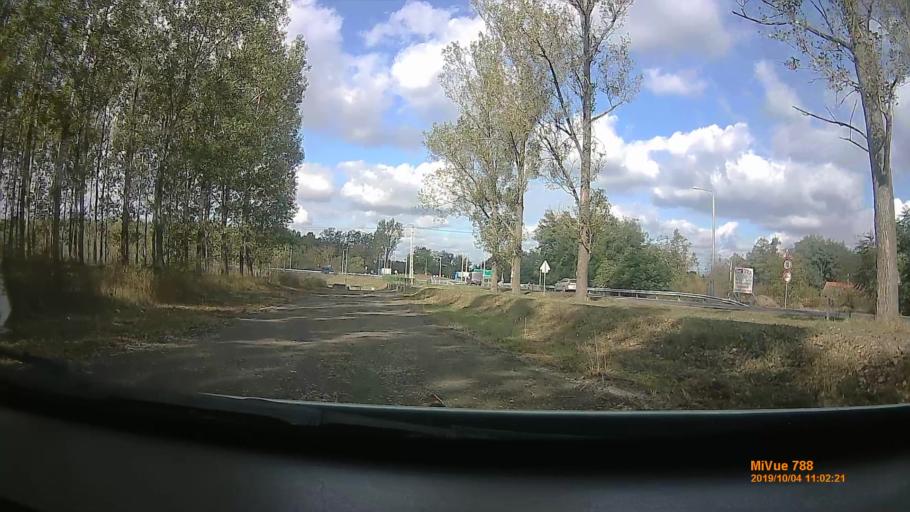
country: HU
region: Szabolcs-Szatmar-Bereg
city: Nyirtelek
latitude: 47.9864
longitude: 21.6726
